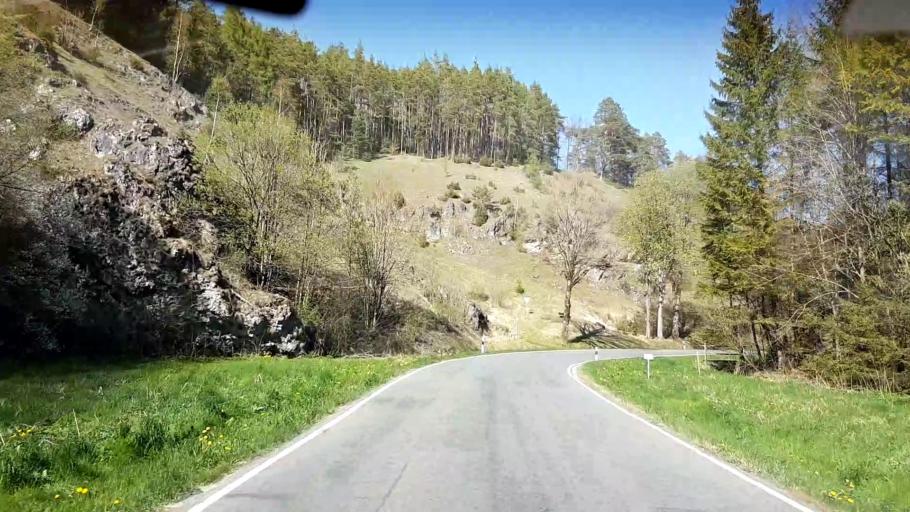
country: DE
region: Bavaria
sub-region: Upper Franconia
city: Pottenstein
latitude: 49.7780
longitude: 11.4183
